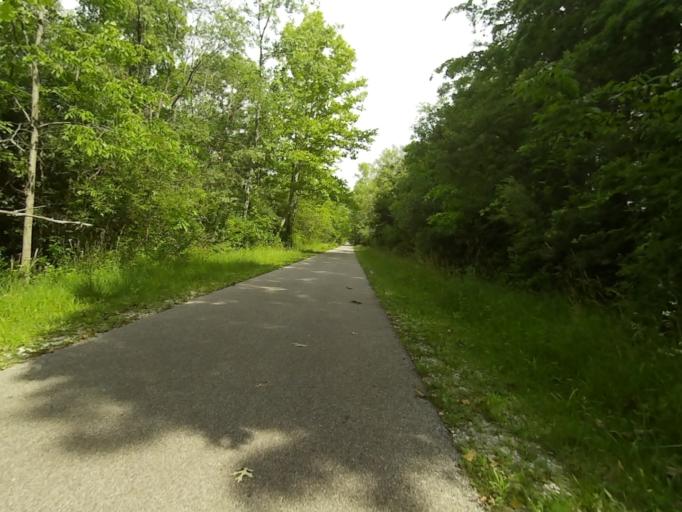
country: US
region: Ohio
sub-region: Summit County
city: Boston Heights
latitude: 41.2868
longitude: -81.5408
